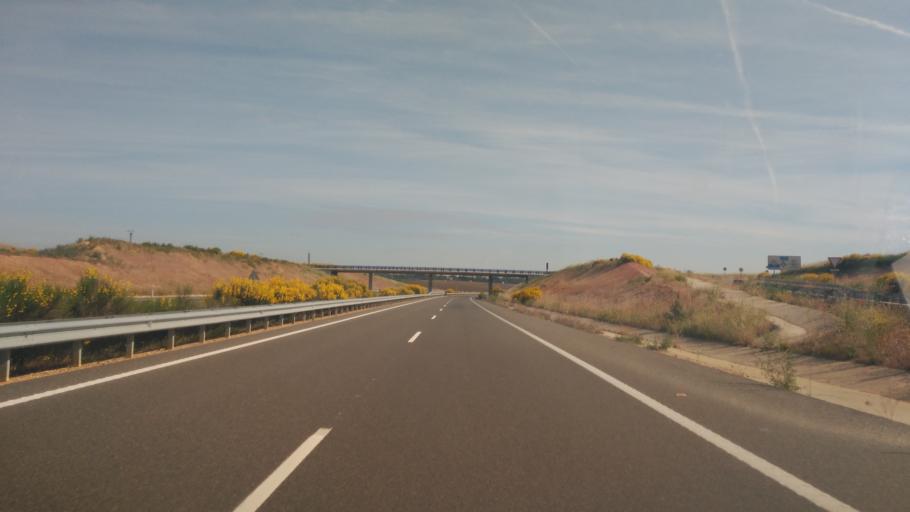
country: ES
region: Castille and Leon
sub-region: Provincia de Salamanca
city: Calzada de Valdunciel
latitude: 41.1201
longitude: -5.6988
